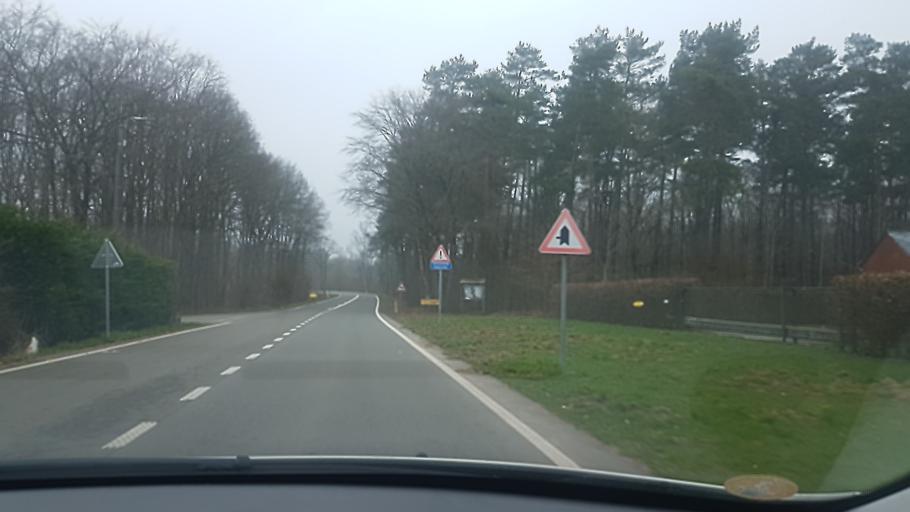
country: FR
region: Champagne-Ardenne
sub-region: Departement des Ardennes
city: Haybes
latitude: 50.0276
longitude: 4.6290
